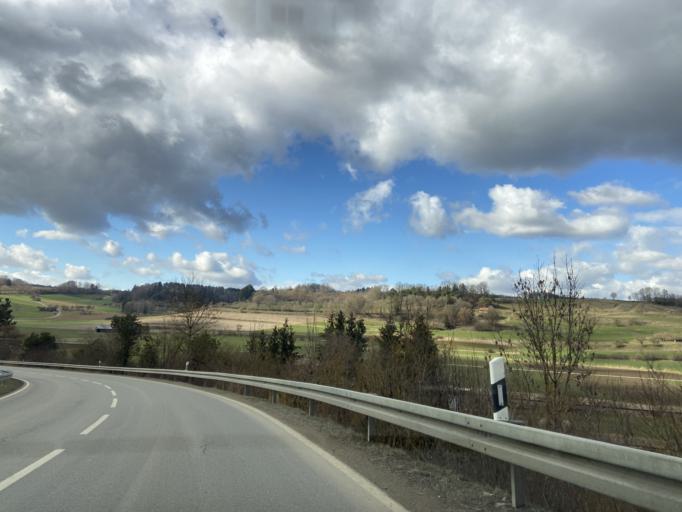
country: DE
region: Baden-Wuerttemberg
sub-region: Tuebingen Region
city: Krauchenwies
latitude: 48.0095
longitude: 9.2063
